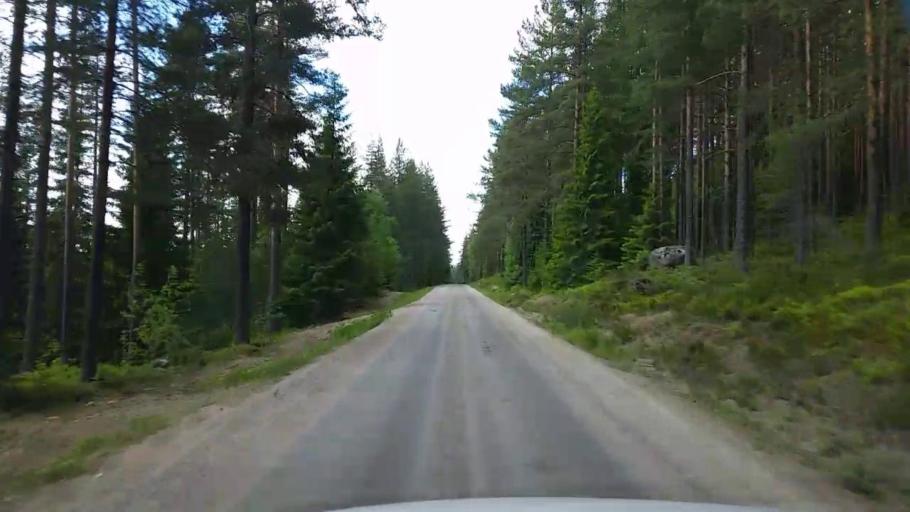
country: SE
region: Gaevleborg
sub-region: Ovanakers Kommun
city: Edsbyn
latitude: 61.5634
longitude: 15.9639
